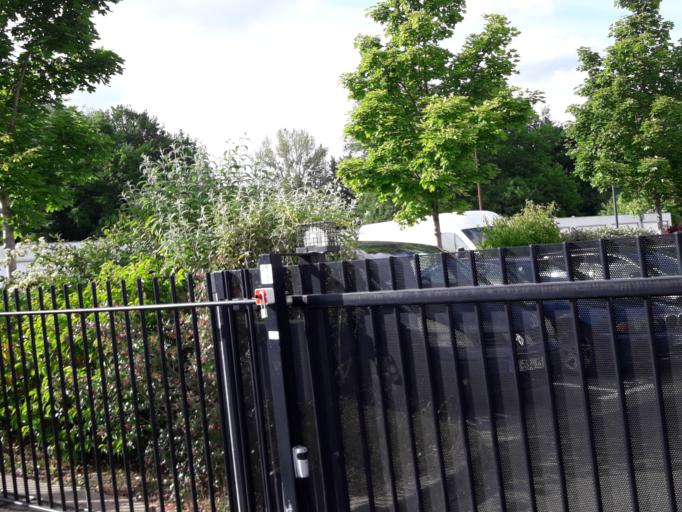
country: FR
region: Ile-de-France
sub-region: Departement de l'Essonne
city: Fleury-Merogis
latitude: 48.6386
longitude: 2.3416
